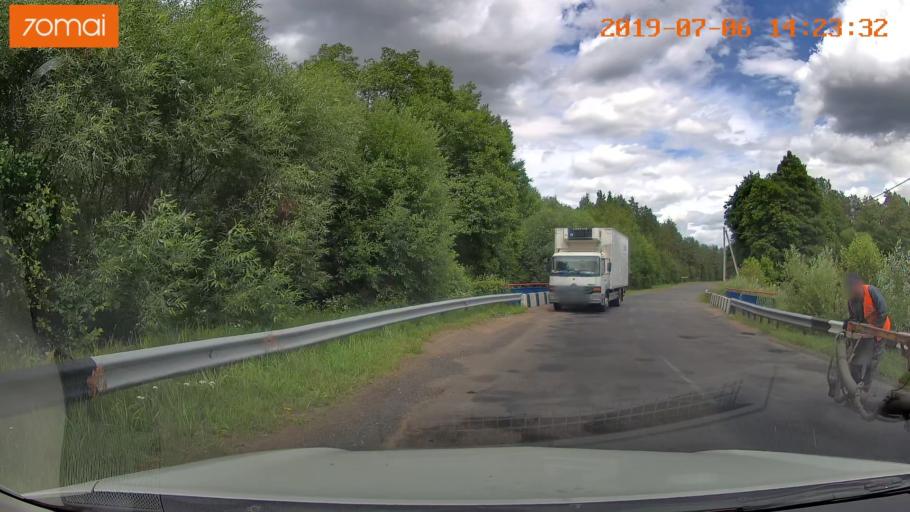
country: BY
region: Minsk
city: Ivyanyets
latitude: 53.9184
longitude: 26.7693
